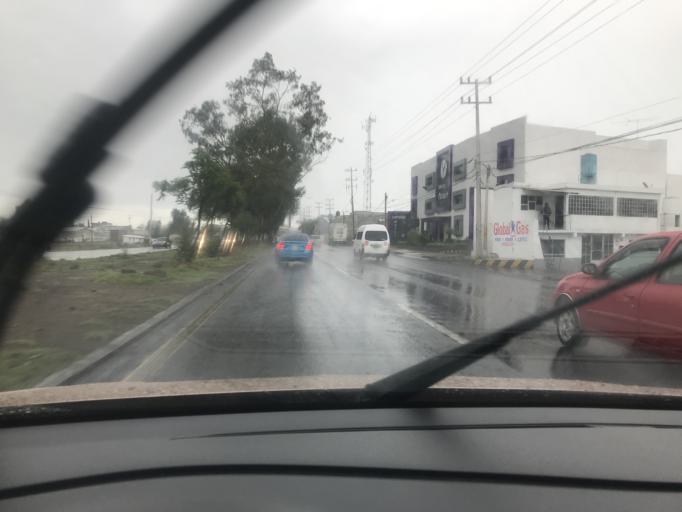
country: MX
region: Mexico
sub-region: Texcoco
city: Colonia Lazaro Cardenas
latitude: 19.4353
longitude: -98.9070
